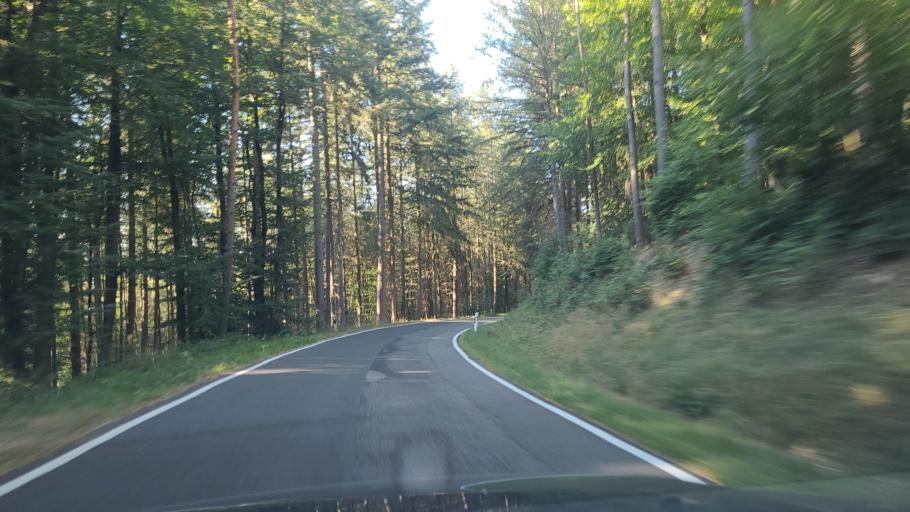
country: DE
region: Rheinland-Pfalz
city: Dierscheid
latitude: 49.9035
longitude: 6.7479
